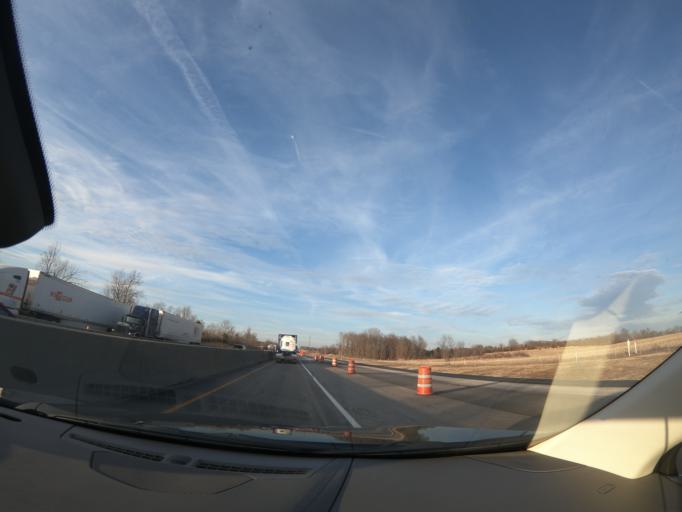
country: US
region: Kentucky
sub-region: Hardin County
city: Elizabethtown
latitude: 37.5895
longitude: -85.8701
